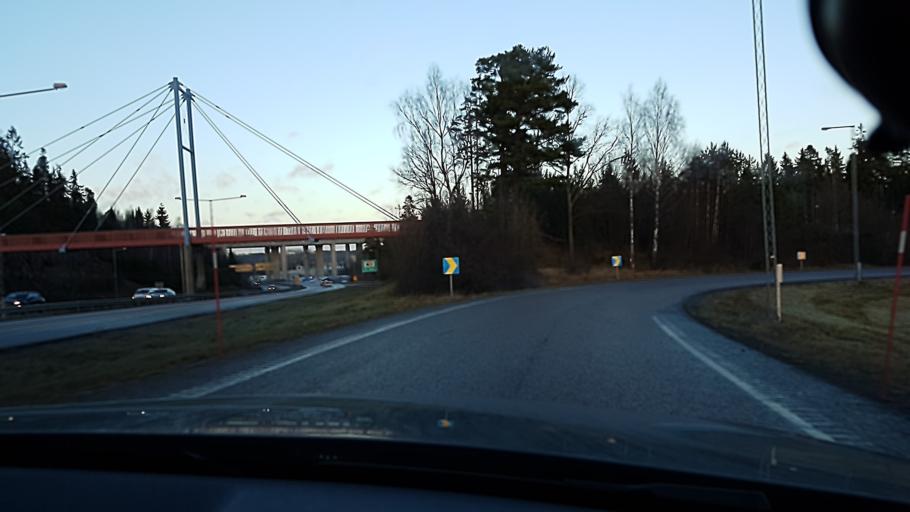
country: SE
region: Stockholm
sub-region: Sodertalje Kommun
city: Pershagen
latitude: 59.1589
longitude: 17.6471
